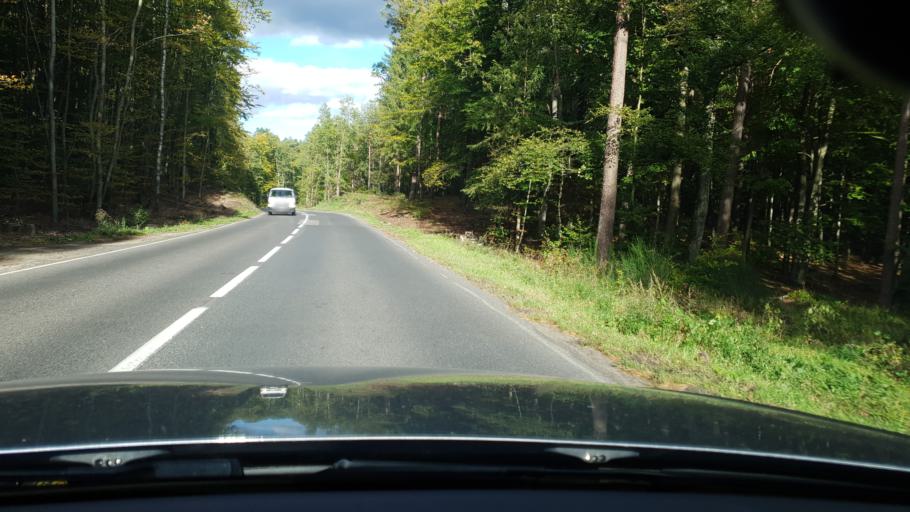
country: PL
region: Pomeranian Voivodeship
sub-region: Powiat wejherowski
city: Koleczkowo
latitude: 54.5017
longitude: 18.3652
